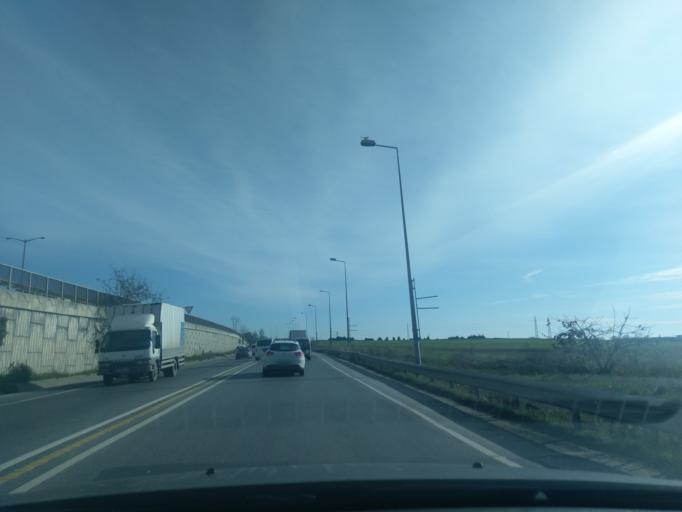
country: TR
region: Istanbul
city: Esenyurt
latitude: 41.0553
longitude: 28.7141
